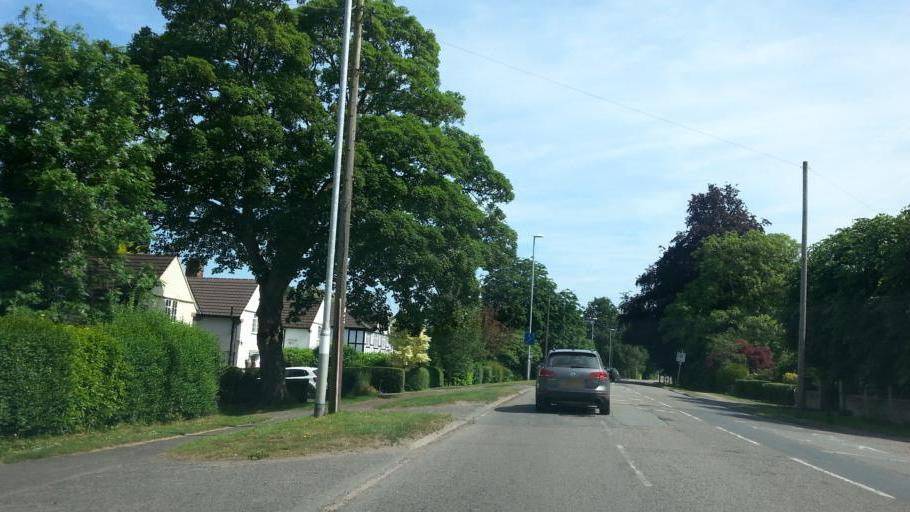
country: GB
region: England
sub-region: Cambridgeshire
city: Grantchester
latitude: 52.1599
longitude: 0.1261
